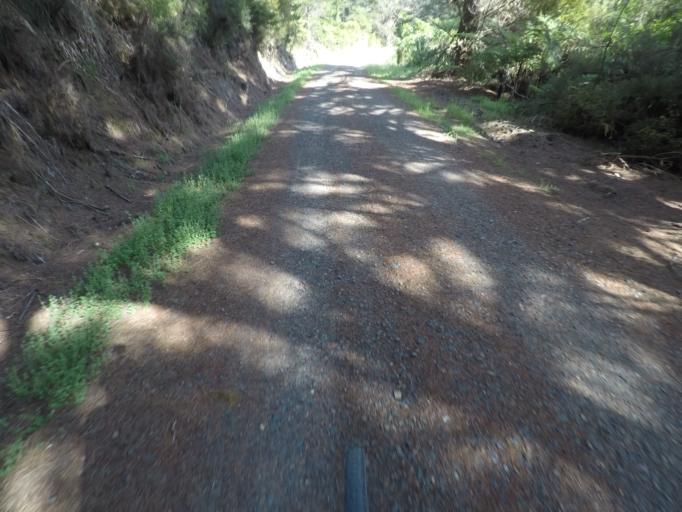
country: NZ
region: Auckland
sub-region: Auckland
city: Muriwai Beach
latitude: -36.7417
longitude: 174.5750
